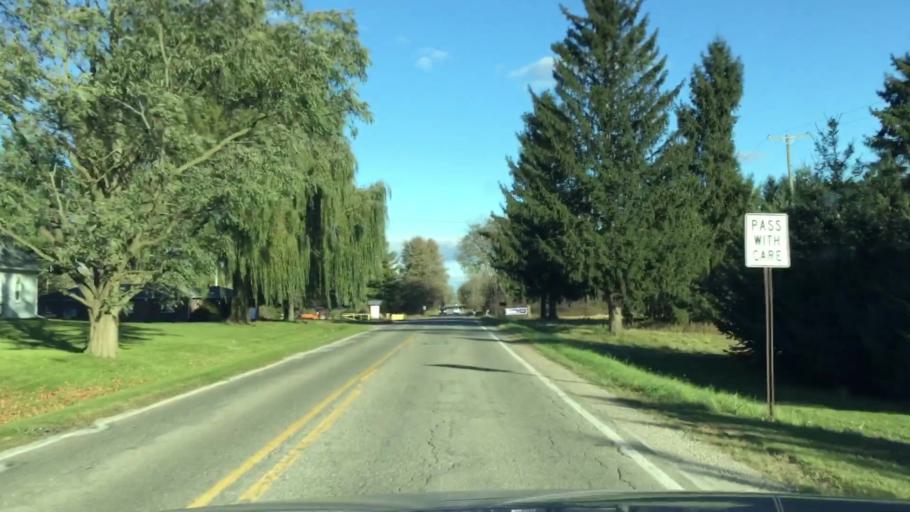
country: US
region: Michigan
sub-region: Lapeer County
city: Lapeer
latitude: 43.0610
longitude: -83.2208
